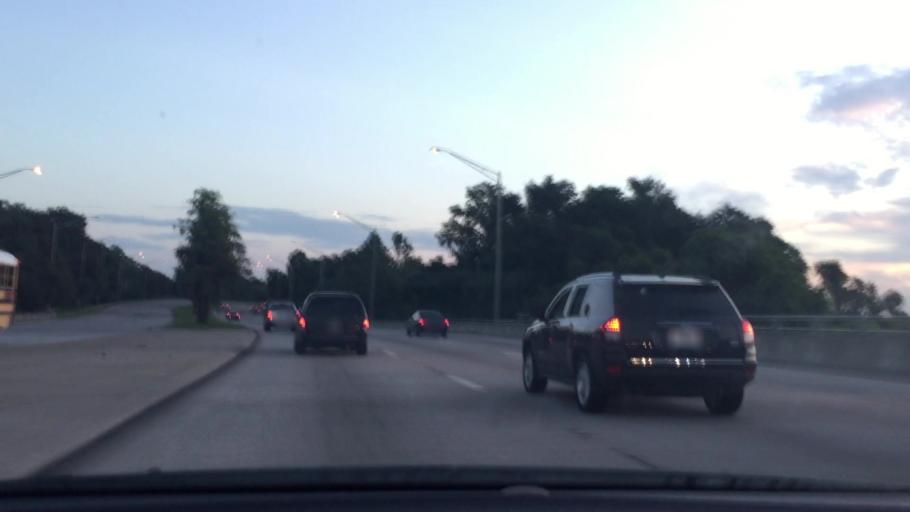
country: US
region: Florida
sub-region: Orange County
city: Holden Heights
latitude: 28.5210
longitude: -81.4175
